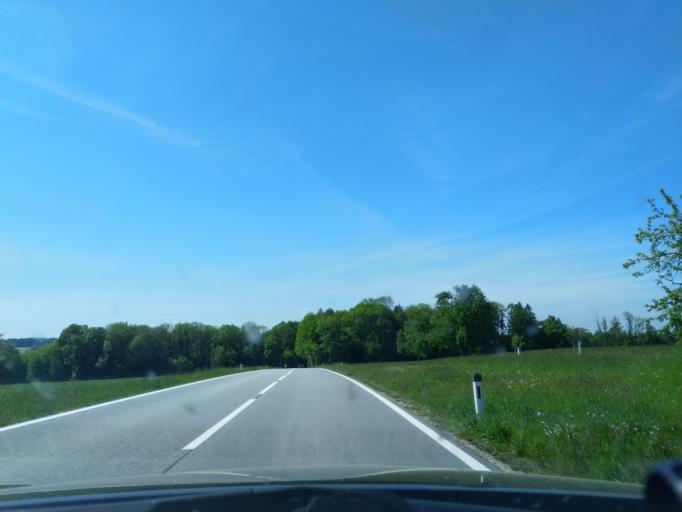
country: AT
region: Upper Austria
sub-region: Politischer Bezirk Ried im Innkreis
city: Ried im Innkreis
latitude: 48.2540
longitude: 13.4322
